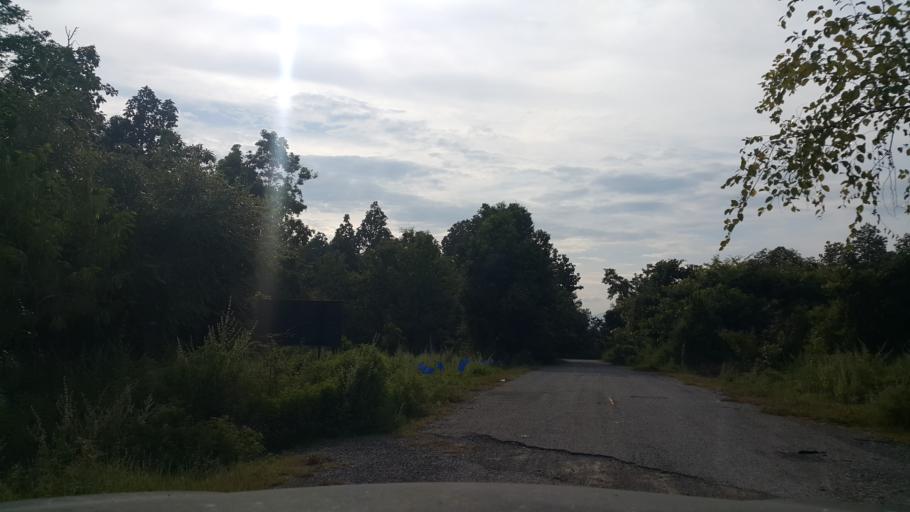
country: TH
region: Chiang Mai
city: San Sai
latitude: 18.9215
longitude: 99.0855
